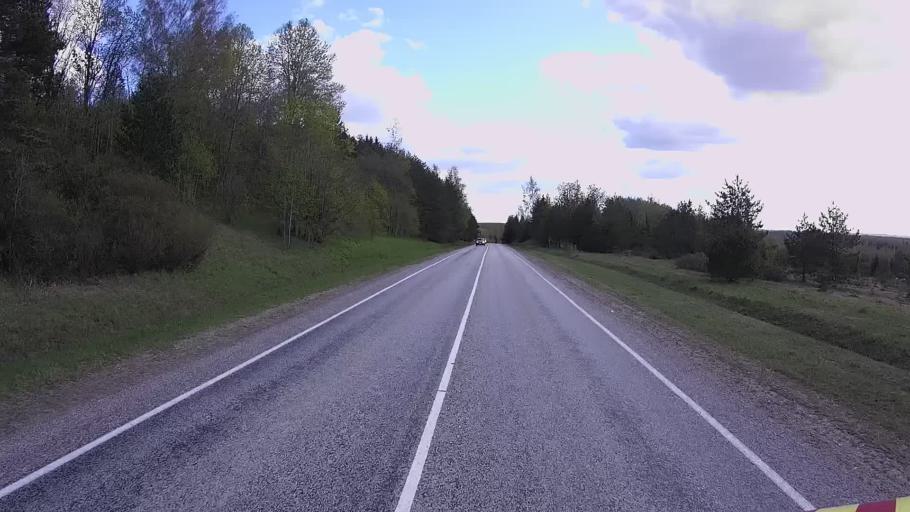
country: EE
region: Jogevamaa
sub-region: Jogeva linn
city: Jogeva
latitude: 58.7807
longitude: 26.4741
